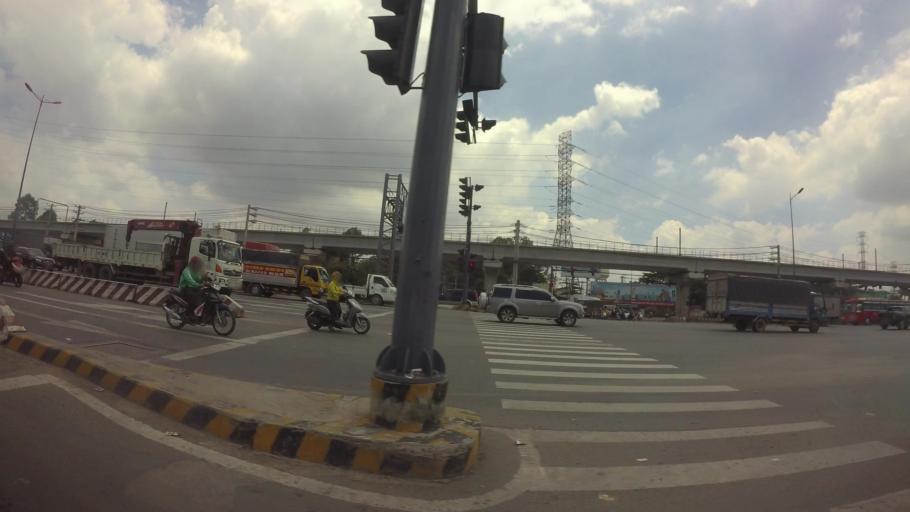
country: VN
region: Ho Chi Minh City
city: Quan Chin
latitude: 10.8272
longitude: 106.7620
